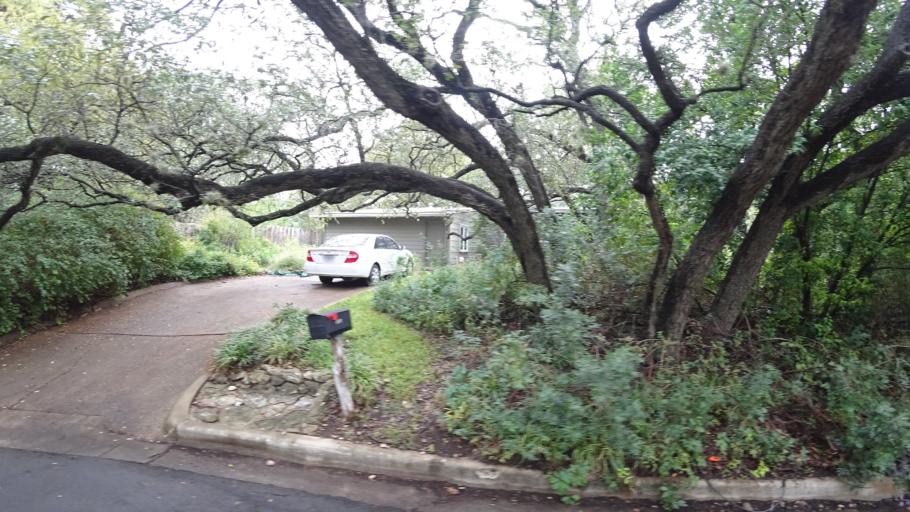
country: US
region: Texas
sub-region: Travis County
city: Rollingwood
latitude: 30.2556
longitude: -97.7785
